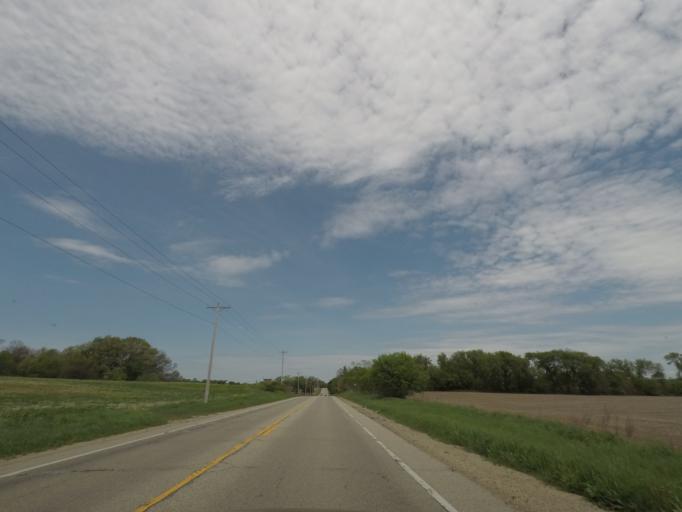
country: US
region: Wisconsin
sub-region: Green County
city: Brooklyn
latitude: 42.8681
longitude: -89.3497
